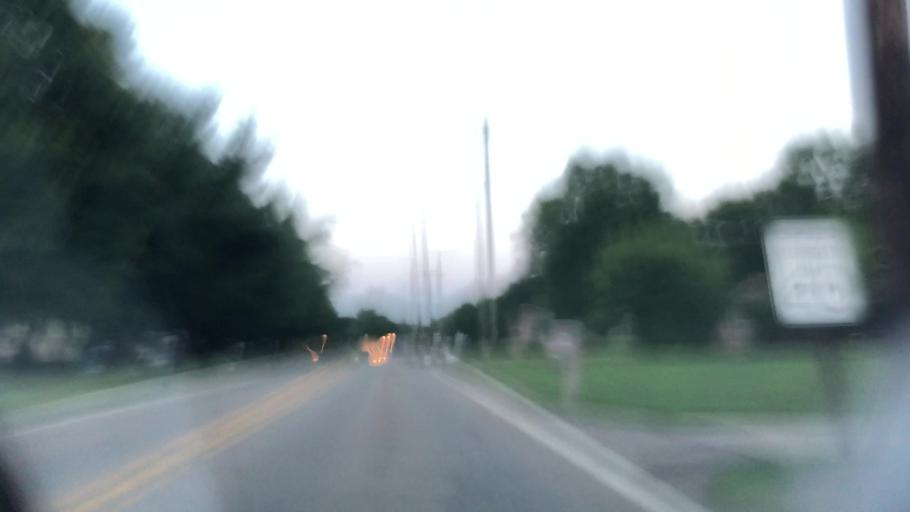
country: US
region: Ohio
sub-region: Stark County
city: Massillon
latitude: 40.8321
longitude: -81.4968
